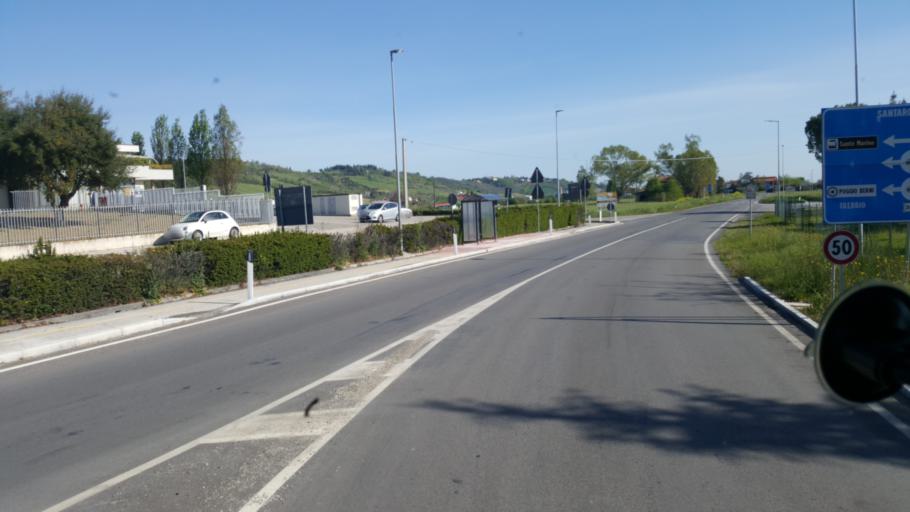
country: IT
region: Emilia-Romagna
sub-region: Provincia di Rimini
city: Poggio Berni
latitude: 44.0045
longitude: 12.4016
